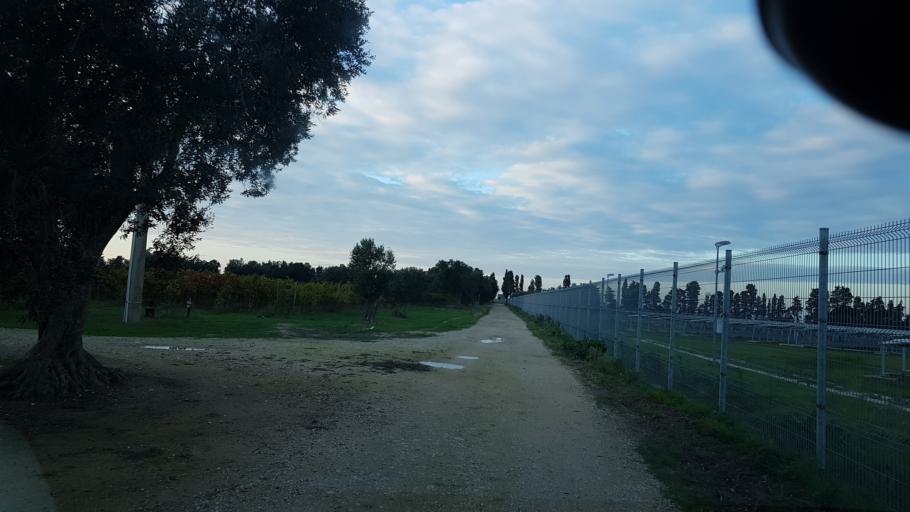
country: IT
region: Apulia
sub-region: Provincia di Brindisi
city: La Rosa
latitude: 40.5927
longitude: 17.9857
